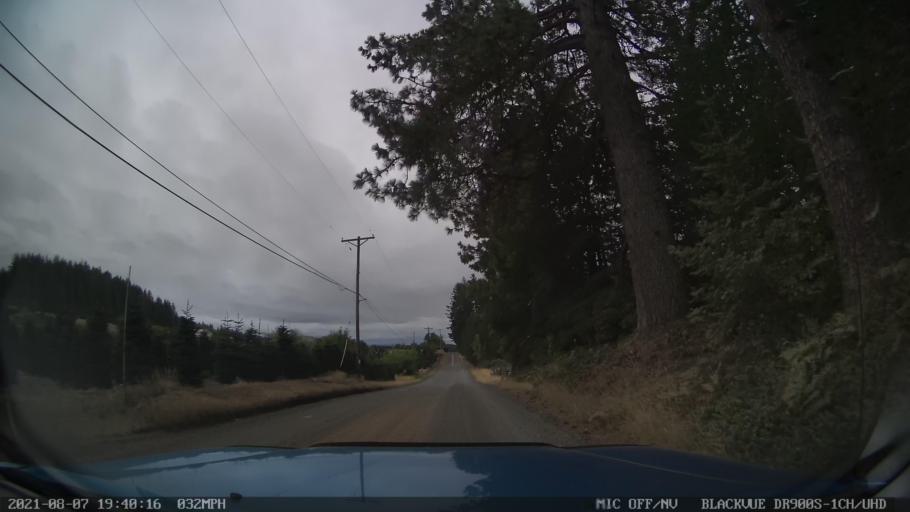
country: US
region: Oregon
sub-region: Marion County
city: Silverton
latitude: 44.9300
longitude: -122.6568
